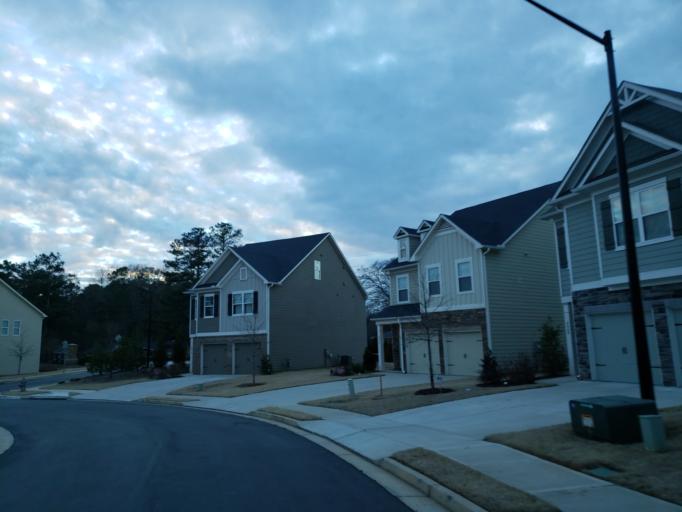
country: US
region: Georgia
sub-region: Cobb County
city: Mableton
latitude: 33.8545
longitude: -84.5878
